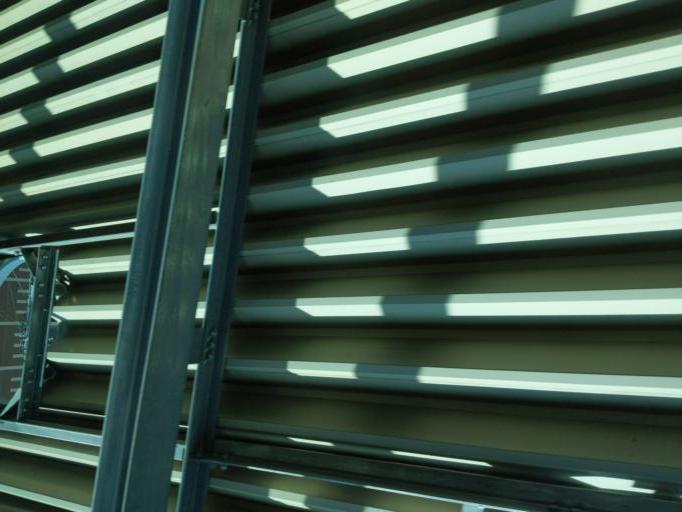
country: JP
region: Tokyo
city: Chofugaoka
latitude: 35.6445
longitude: 139.5023
